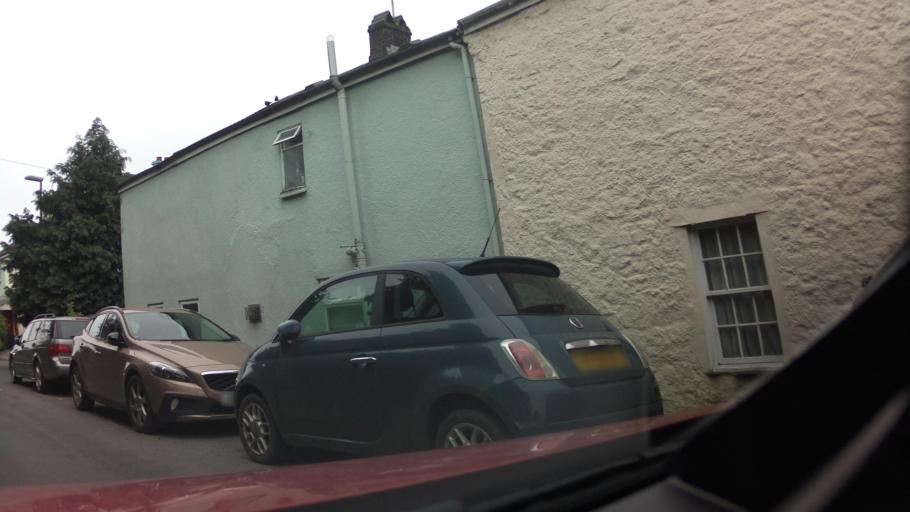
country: GB
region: England
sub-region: Devon
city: Ashburton
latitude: 50.5178
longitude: -3.7503
